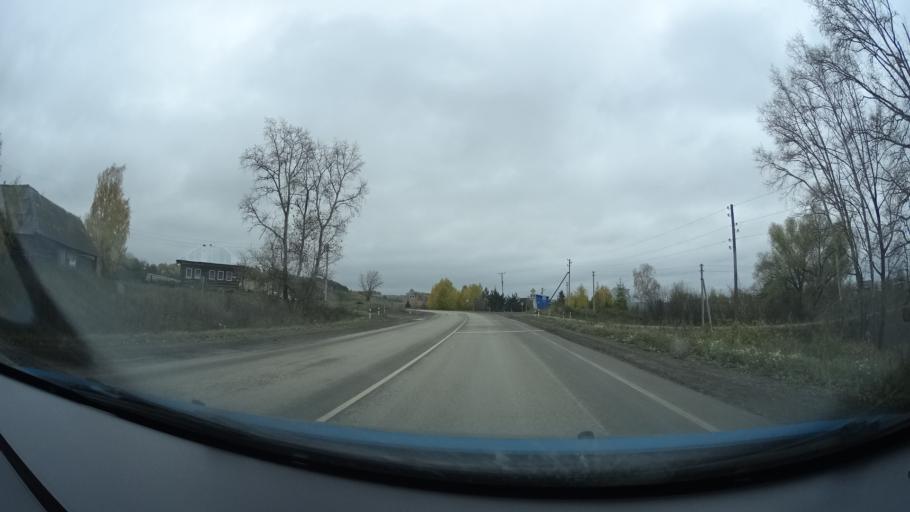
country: RU
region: Perm
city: Osa
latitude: 57.2244
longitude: 55.5875
